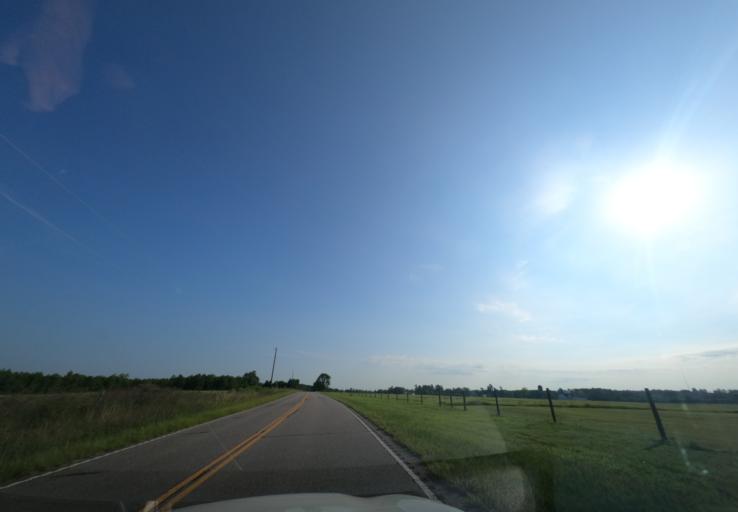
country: US
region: South Carolina
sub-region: Edgefield County
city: Murphys Estates
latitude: 33.6065
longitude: -81.9693
